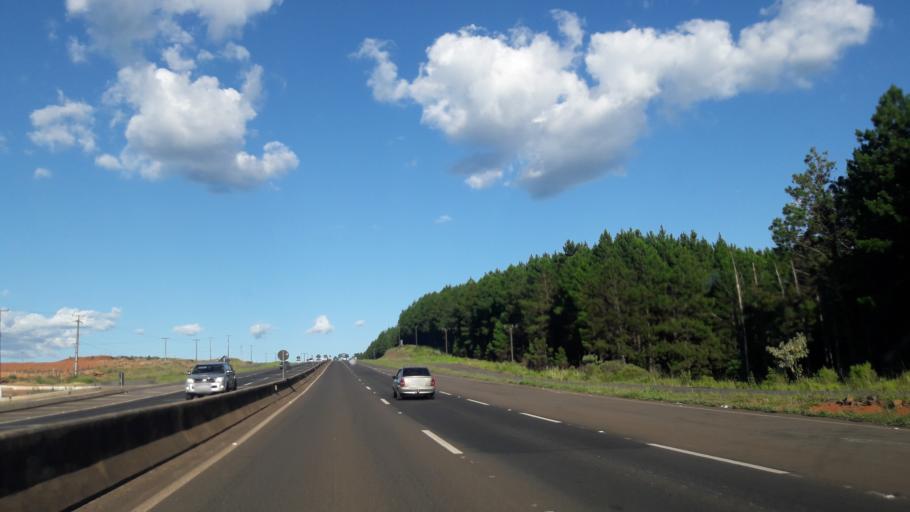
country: BR
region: Parana
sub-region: Guarapuava
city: Guarapuava
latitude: -25.3445
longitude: -51.4412
